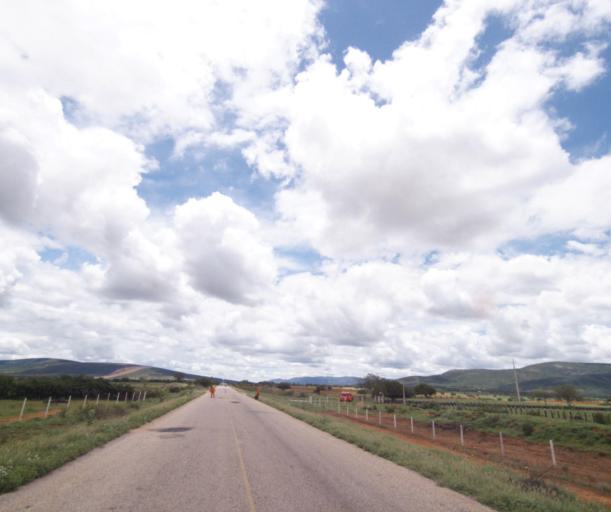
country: BR
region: Bahia
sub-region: Brumado
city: Brumado
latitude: -14.1591
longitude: -41.5252
